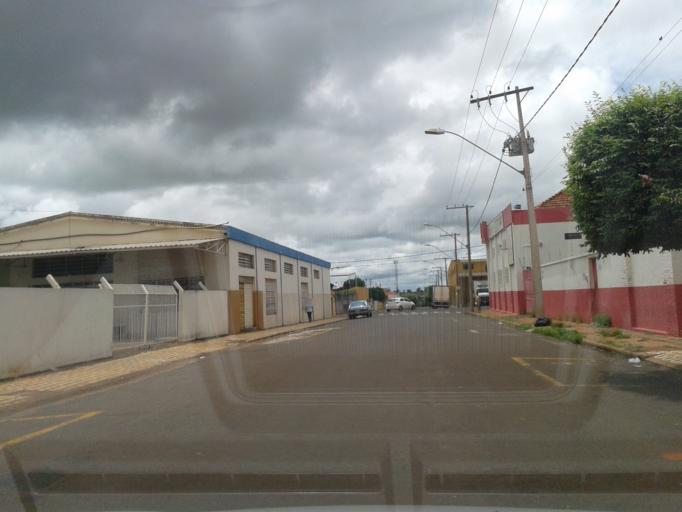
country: BR
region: Minas Gerais
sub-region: Ituiutaba
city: Ituiutaba
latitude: -18.9810
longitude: -49.4579
